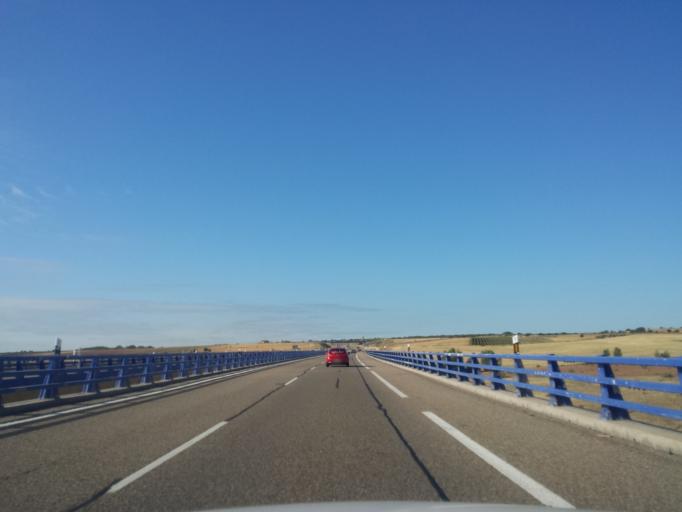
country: ES
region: Castille and Leon
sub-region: Provincia de Leon
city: Valdevimbre
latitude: 42.4122
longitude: -5.5880
